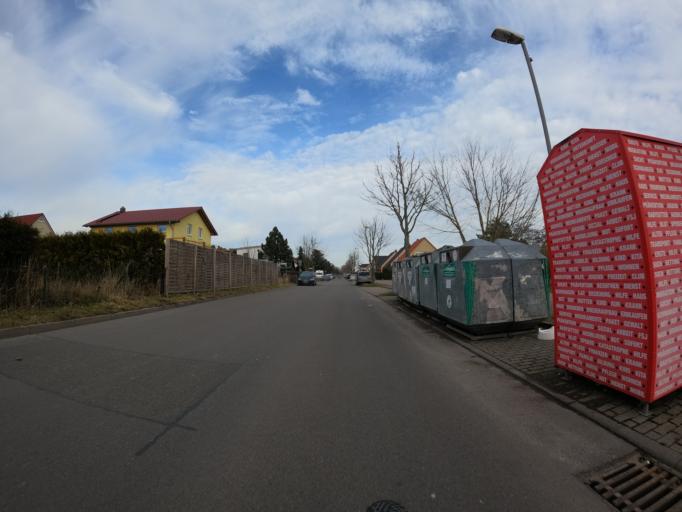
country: DE
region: Berlin
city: Mahlsdorf
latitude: 52.5190
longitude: 13.6341
